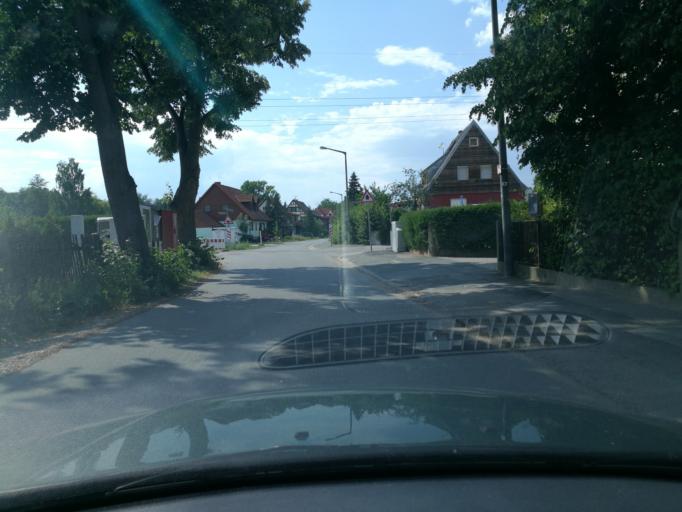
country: DE
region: Bavaria
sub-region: Regierungsbezirk Mittelfranken
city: Erlangen
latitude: 49.5345
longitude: 11.0006
